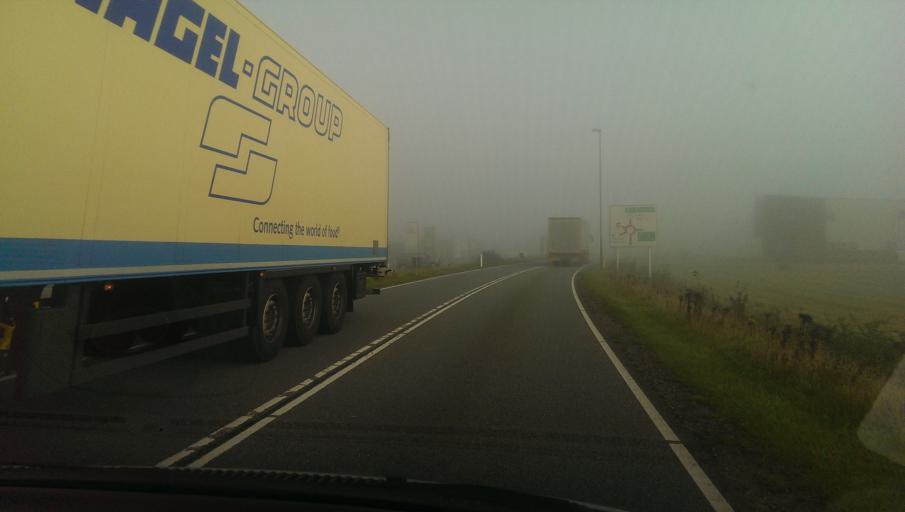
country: DK
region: South Denmark
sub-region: Vejen Kommune
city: Vejen
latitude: 55.4914
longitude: 9.1300
